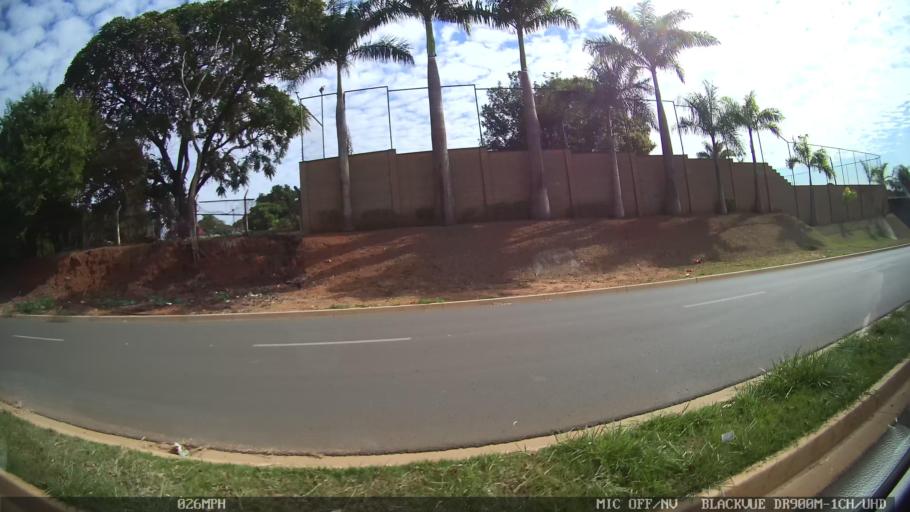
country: BR
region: Sao Paulo
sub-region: Santa Barbara D'Oeste
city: Santa Barbara d'Oeste
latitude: -22.7785
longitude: -47.4038
